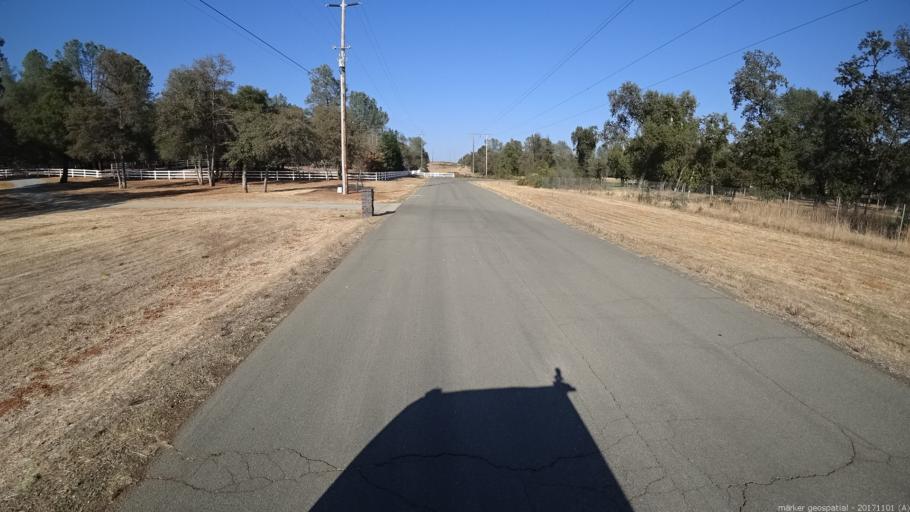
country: US
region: California
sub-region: Shasta County
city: Shasta Lake
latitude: 40.6785
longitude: -122.3296
